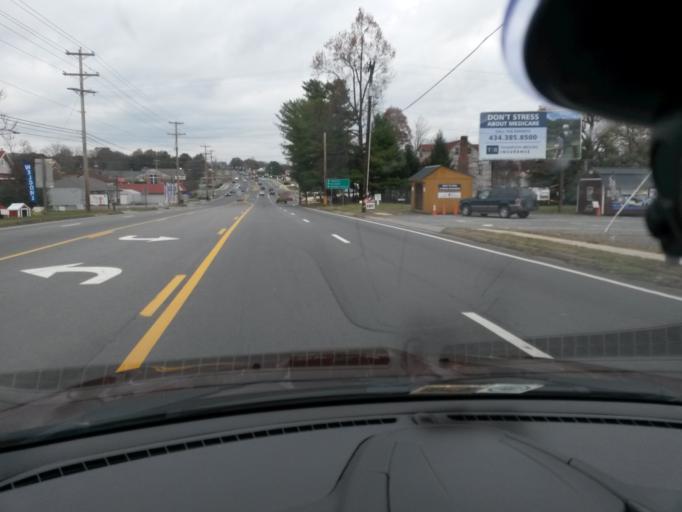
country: US
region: Virginia
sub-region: Amherst County
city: Madison Heights
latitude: 37.4645
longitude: -79.1187
